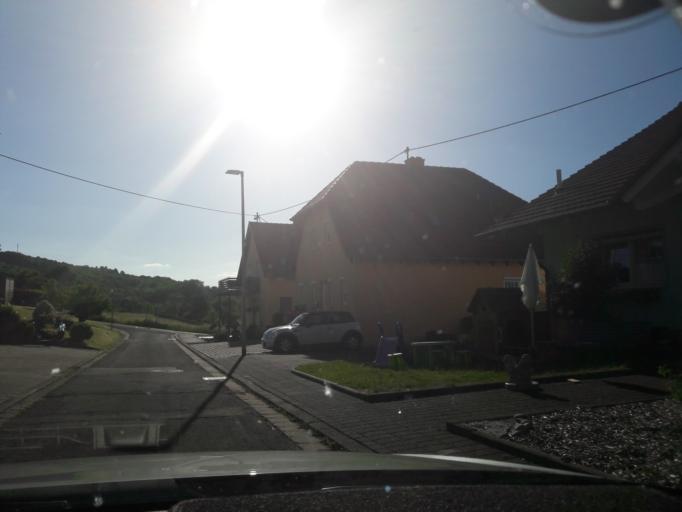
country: DE
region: Saarland
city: Sankt Wendel
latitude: 49.4490
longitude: 7.1544
